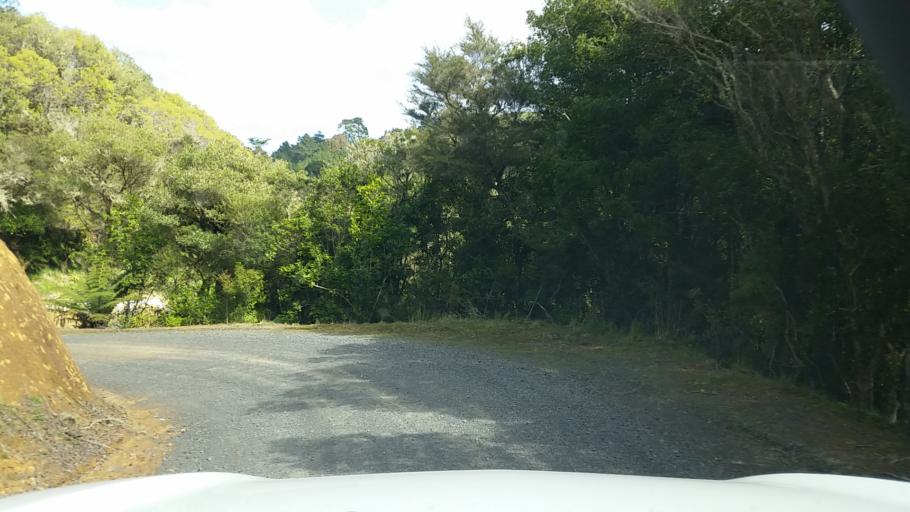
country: NZ
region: Waikato
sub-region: Hauraki District
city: Ngatea
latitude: -37.4664
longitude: 175.4562
